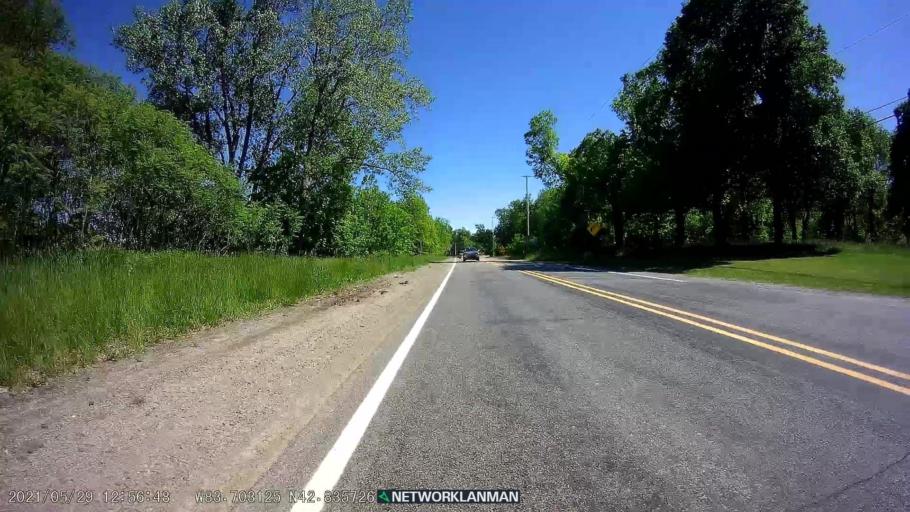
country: US
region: Michigan
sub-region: Genesee County
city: Lake Fenton
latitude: 42.8358
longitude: -83.7030
